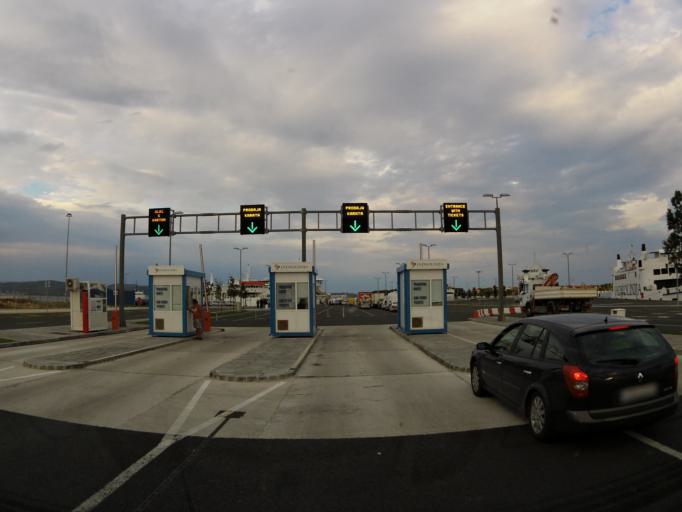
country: HR
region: Zadarska
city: Zadar
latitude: 44.0936
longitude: 15.2582
